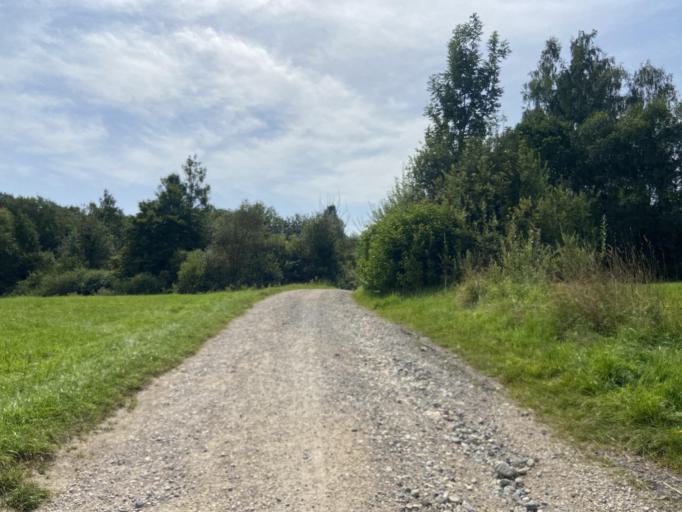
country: DE
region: Baden-Wuerttemberg
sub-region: Tuebingen Region
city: Sigmaringen
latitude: 48.1017
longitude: 9.2342
